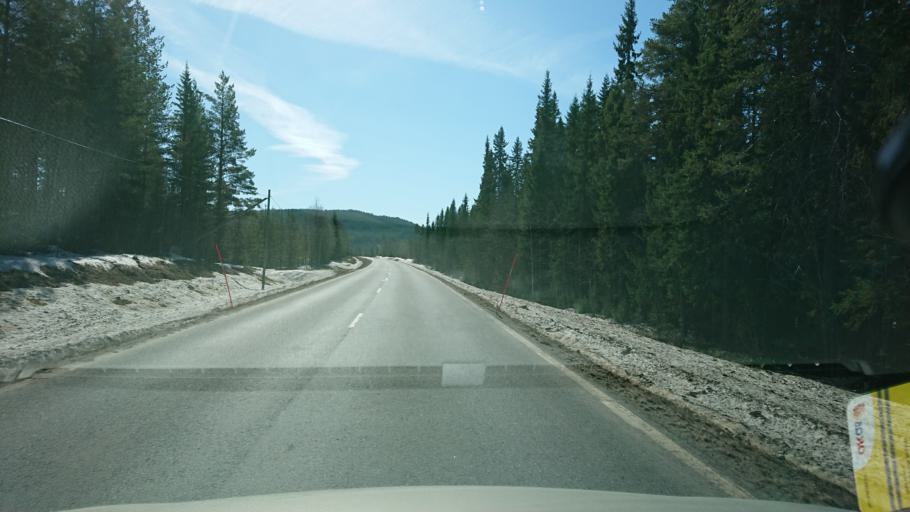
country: SE
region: Vaesterbotten
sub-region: Dorotea Kommun
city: Dorotea
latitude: 64.0649
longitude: 16.2585
